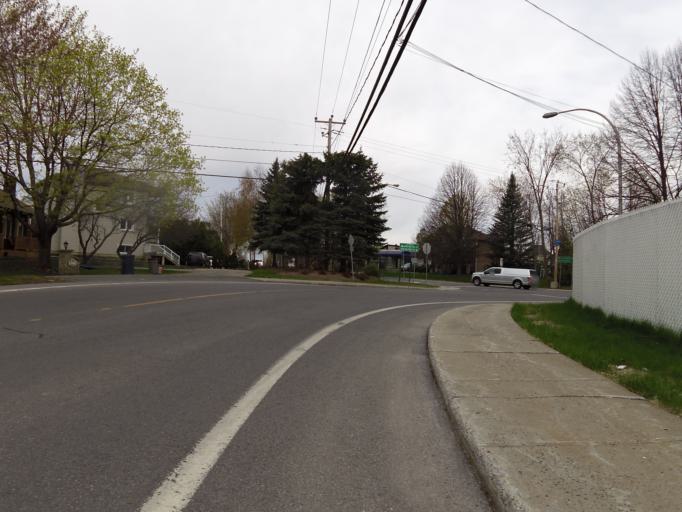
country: CA
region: Quebec
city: Dollard-Des Ormeaux
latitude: 45.5207
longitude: -73.8243
